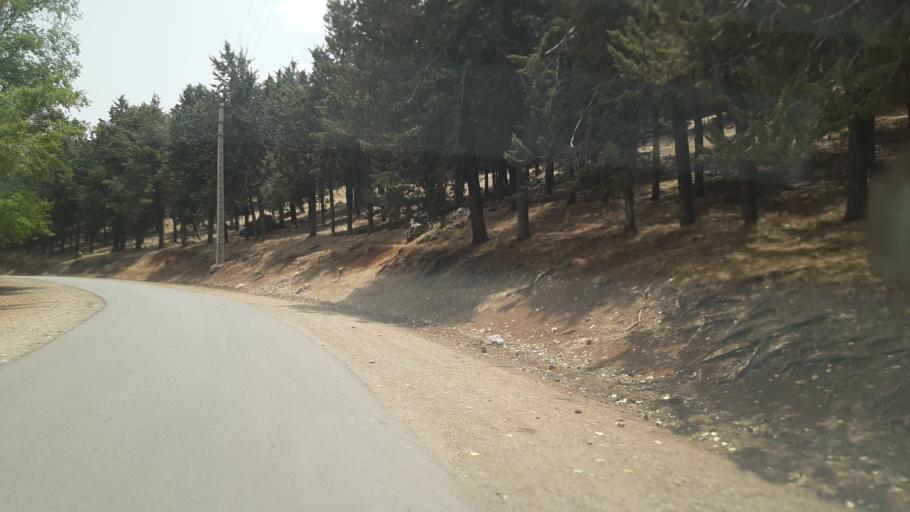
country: MA
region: Meknes-Tafilalet
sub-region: Ifrane
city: Ifrane
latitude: 33.6534
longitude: -5.0441
